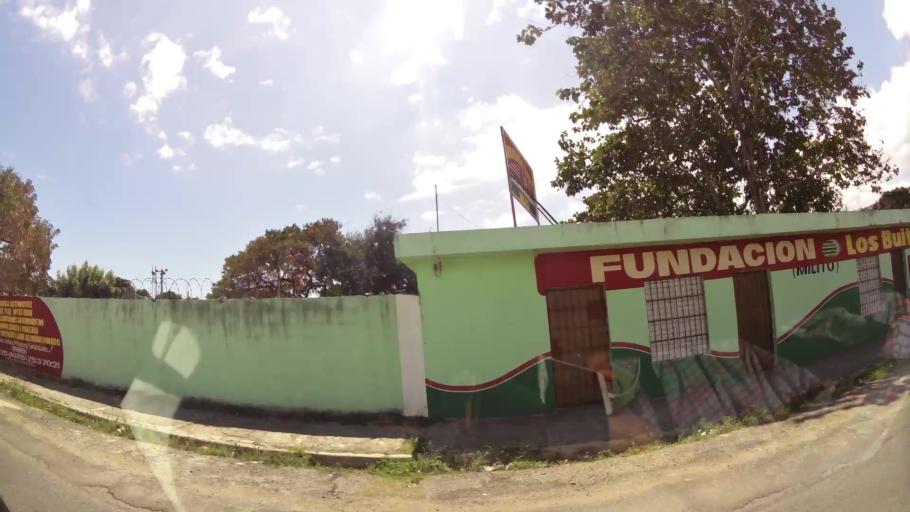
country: DO
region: San Cristobal
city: San Cristobal
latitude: 18.4092
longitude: -70.1084
